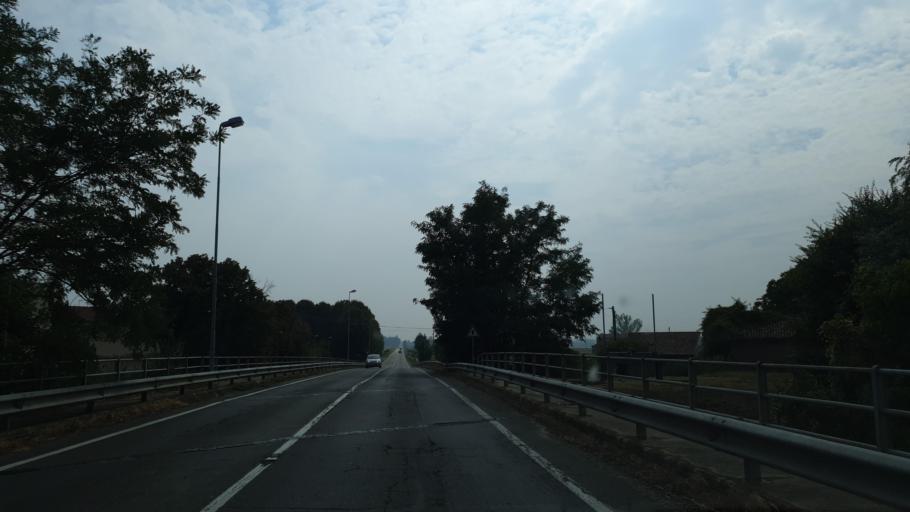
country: IT
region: Emilia-Romagna
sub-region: Provincia di Parma
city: San Secondo Parmense
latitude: 44.9504
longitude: 10.2195
